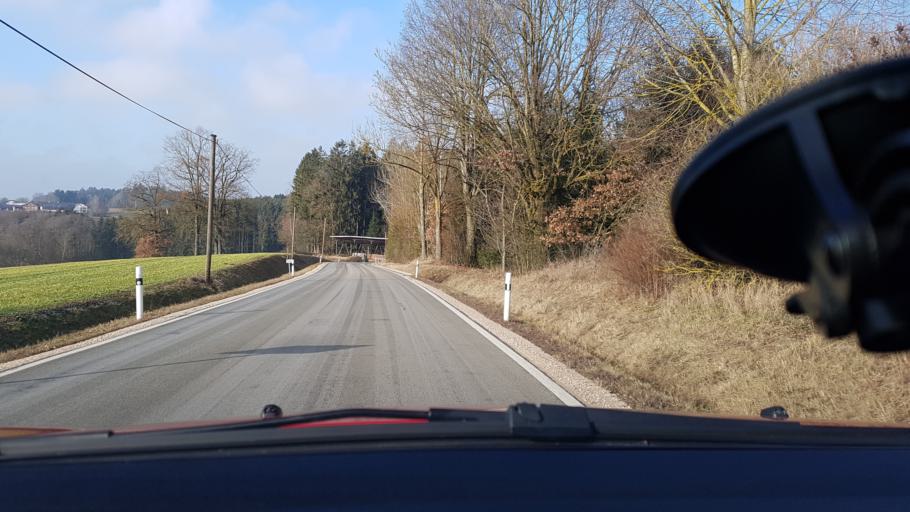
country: DE
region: Bavaria
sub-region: Lower Bavaria
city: Wittibreut
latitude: 48.3306
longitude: 12.9799
